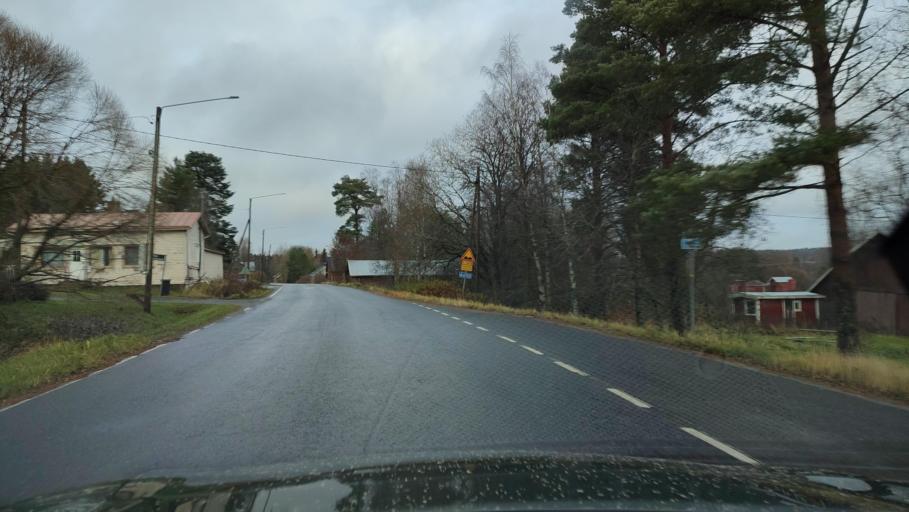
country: FI
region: Southern Ostrobothnia
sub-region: Suupohja
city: Karijoki
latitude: 62.3808
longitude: 21.5574
